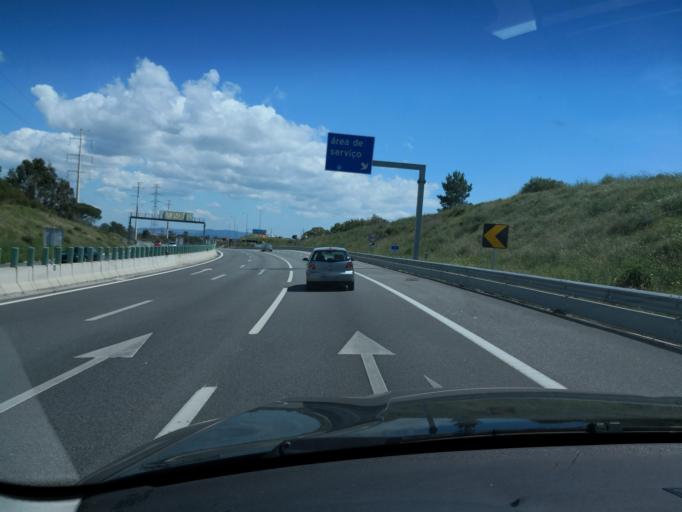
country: PT
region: Setubal
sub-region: Almada
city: Sobreda
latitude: 38.6397
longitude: -9.2010
